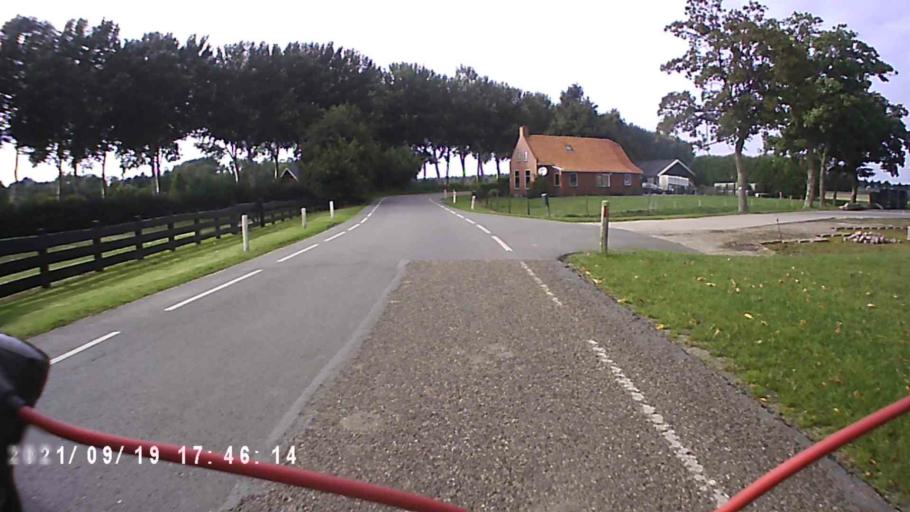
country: NL
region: Groningen
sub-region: Gemeente Delfzijl
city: Delfzijl
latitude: 53.2599
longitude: 6.9541
